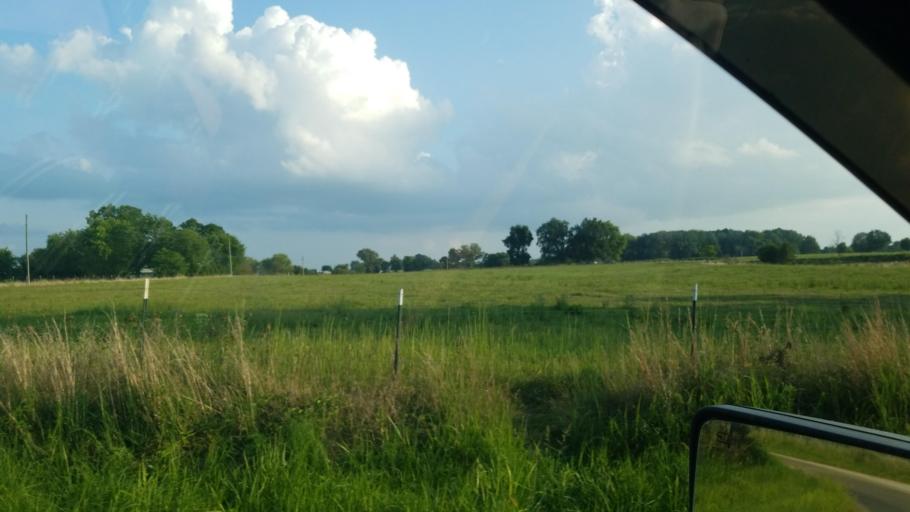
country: US
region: Illinois
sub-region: Saline County
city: Harrisburg
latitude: 37.7847
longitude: -88.6017
